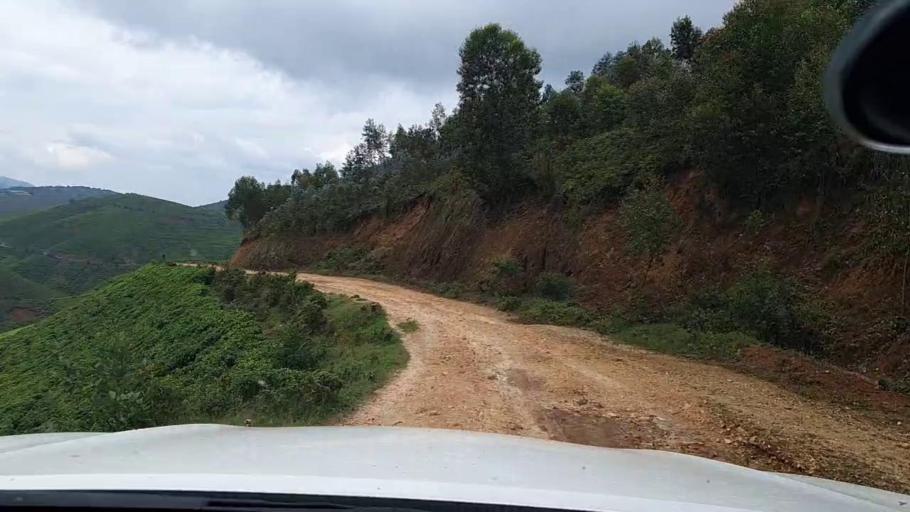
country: RW
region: Western Province
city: Kibuye
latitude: -2.1581
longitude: 29.4535
